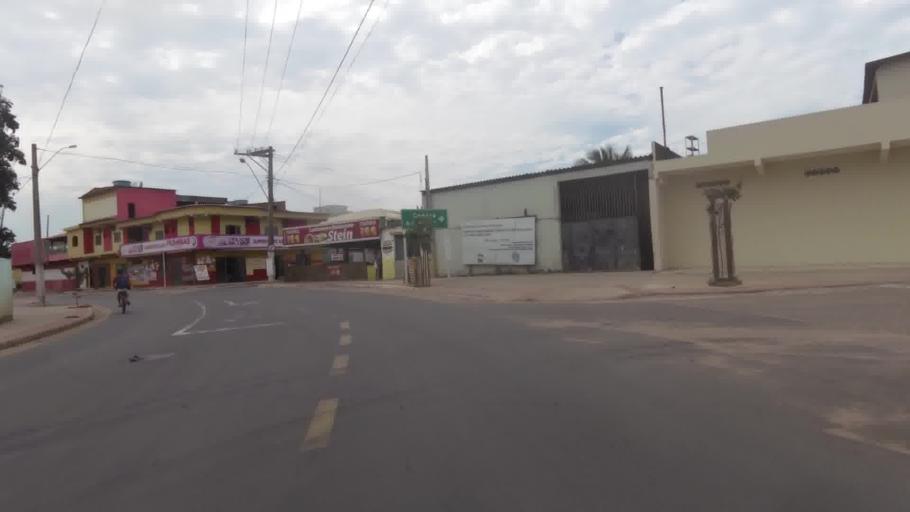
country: BR
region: Espirito Santo
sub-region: Piuma
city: Piuma
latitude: -20.8434
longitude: -40.7443
